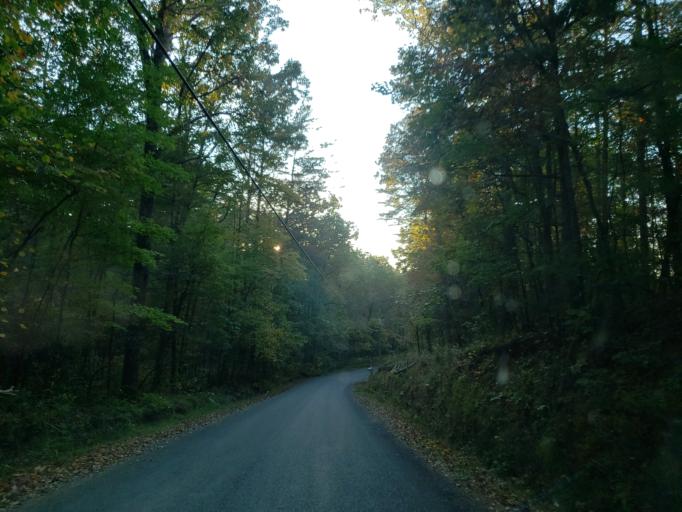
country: US
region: Georgia
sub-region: Gilmer County
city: Ellijay
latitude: 34.6490
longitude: -84.2846
